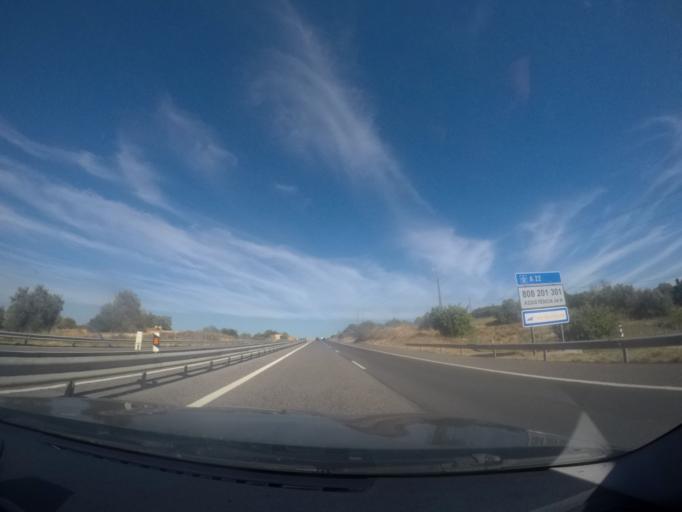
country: PT
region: Faro
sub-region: Lagoa
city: Estombar
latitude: 37.1605
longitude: -8.4994
